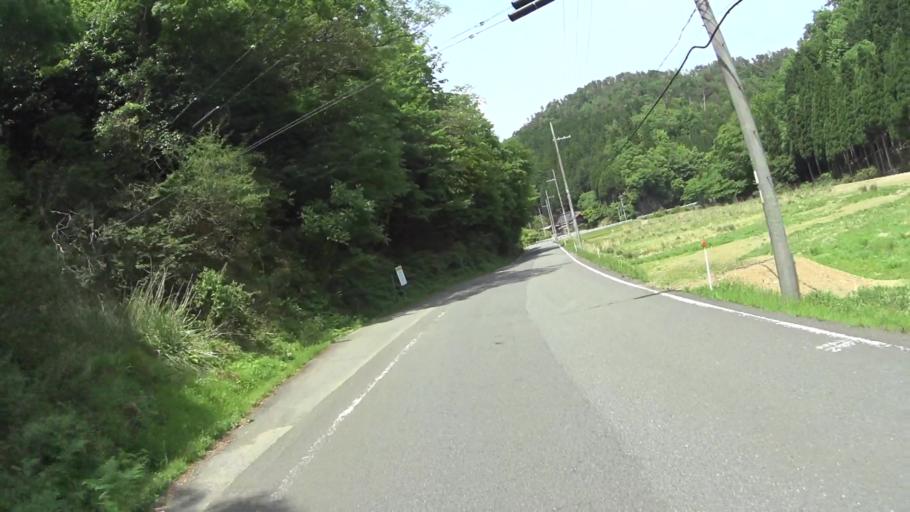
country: JP
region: Kyoto
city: Maizuru
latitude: 35.4160
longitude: 135.4632
